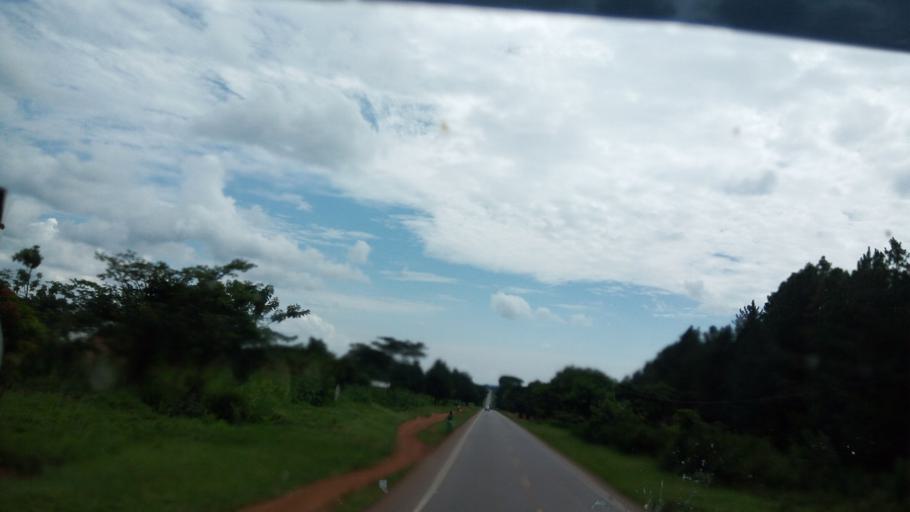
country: UG
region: Central Region
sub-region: Nakasongola District
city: Nakasongola
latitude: 1.1970
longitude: 32.4620
